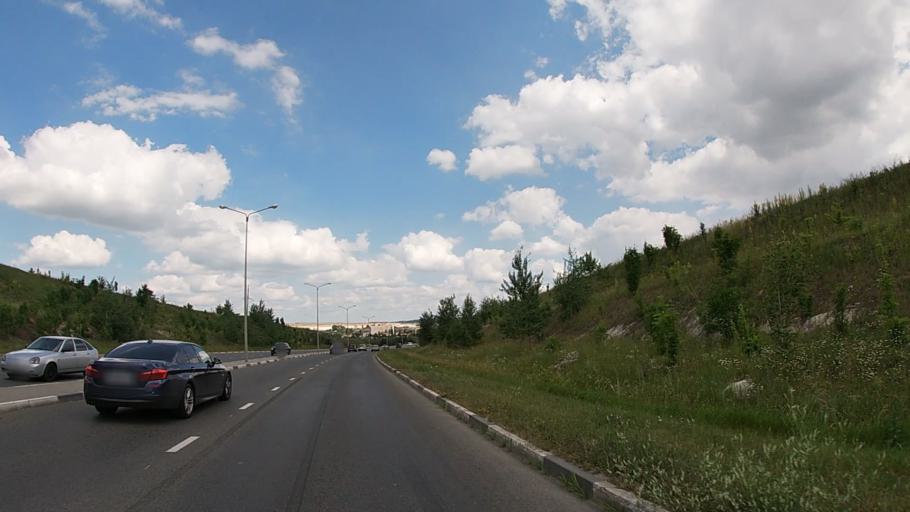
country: RU
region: Belgorod
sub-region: Belgorodskiy Rayon
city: Belgorod
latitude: 50.6033
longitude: 36.5298
